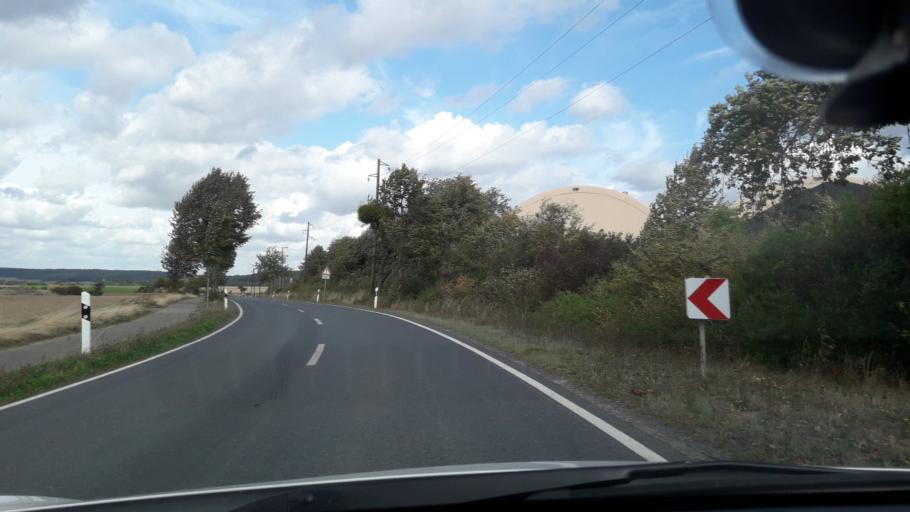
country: DE
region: Lower Saxony
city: Alt Wallmoden
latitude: 52.0612
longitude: 10.3330
